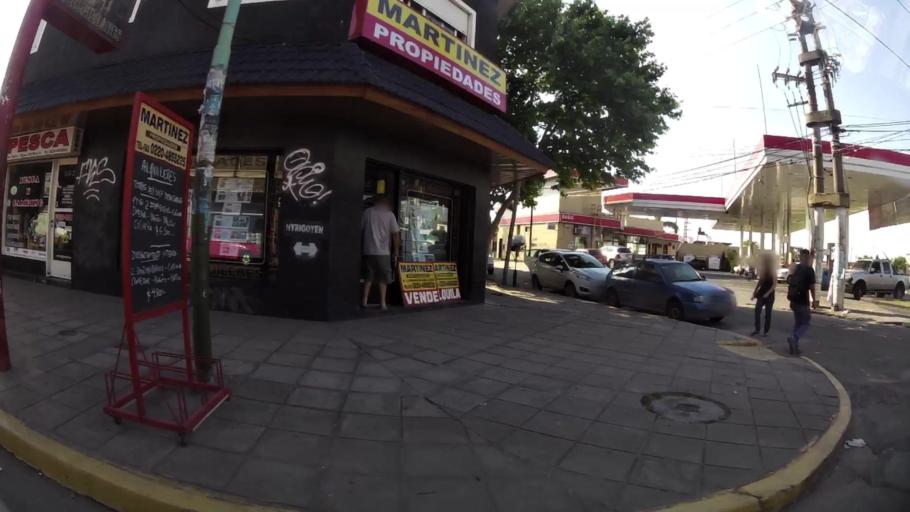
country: AR
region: Buenos Aires
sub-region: Partido de Merlo
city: Merlo
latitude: -34.6594
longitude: -58.7254
